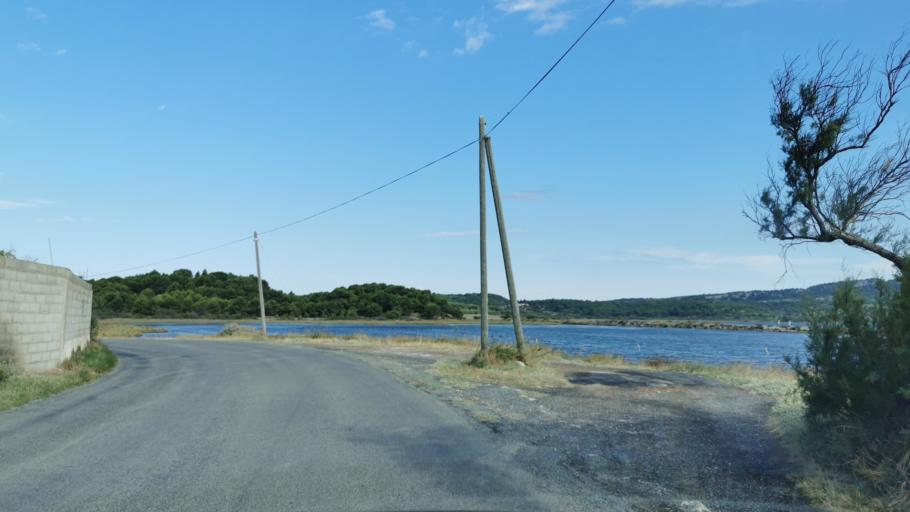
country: FR
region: Languedoc-Roussillon
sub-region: Departement de l'Aude
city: Gruissan
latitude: 43.1063
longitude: 3.0792
